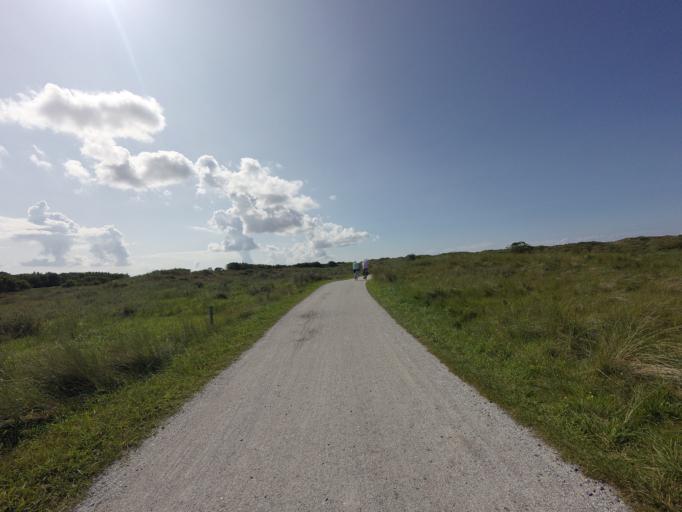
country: NL
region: Friesland
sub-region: Gemeente Terschelling
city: West-Terschelling
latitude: 53.4097
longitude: 5.3998
